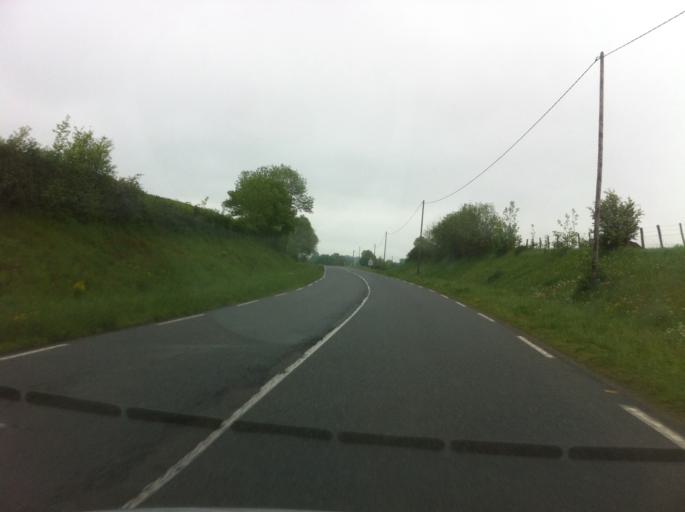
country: FR
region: Auvergne
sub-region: Departement de l'Allier
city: Chantelle
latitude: 46.3194
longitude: 3.1032
